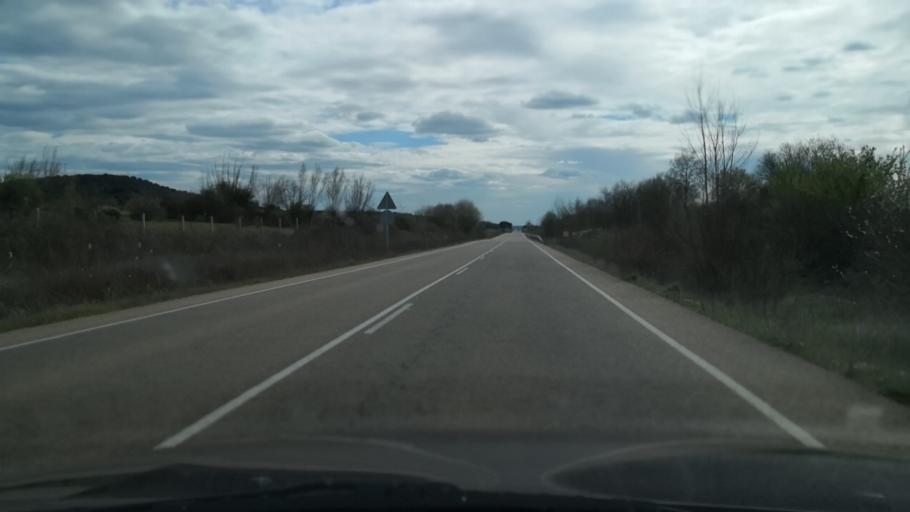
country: ES
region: Castille and Leon
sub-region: Provincia de Salamanca
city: Ciudad Rodrigo
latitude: 40.5783
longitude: -6.5384
